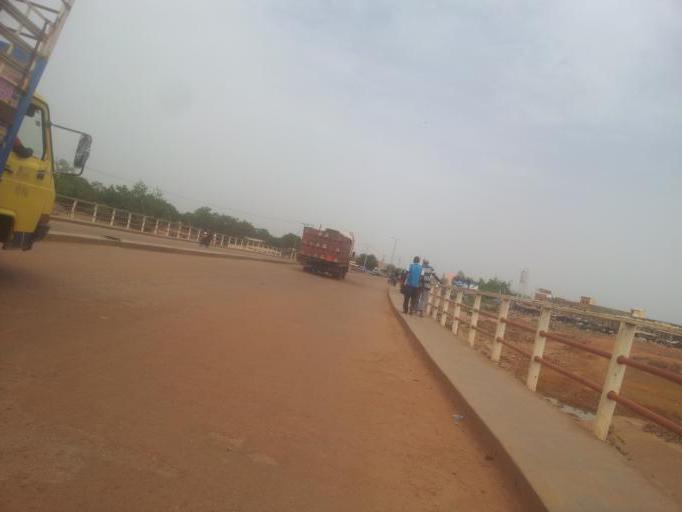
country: BF
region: Centre
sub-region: Kadiogo Province
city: Ouagadougou
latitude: 12.3846
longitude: -1.5546
